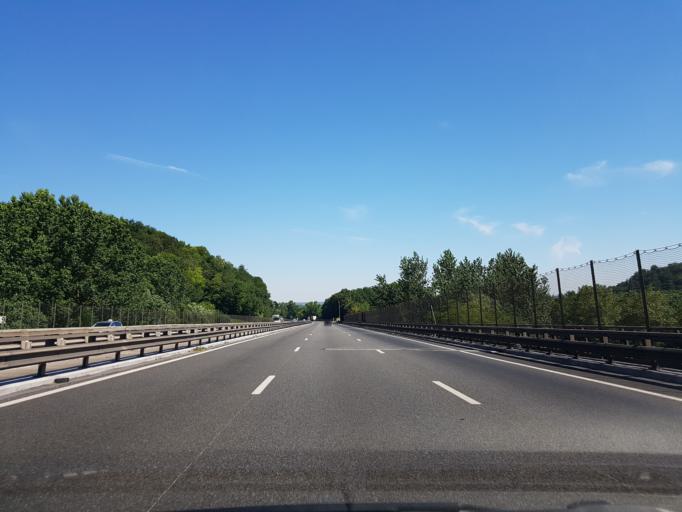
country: FR
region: Picardie
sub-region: Departement de l'Oise
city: Pontpoint
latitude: 49.2957
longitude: 2.6904
